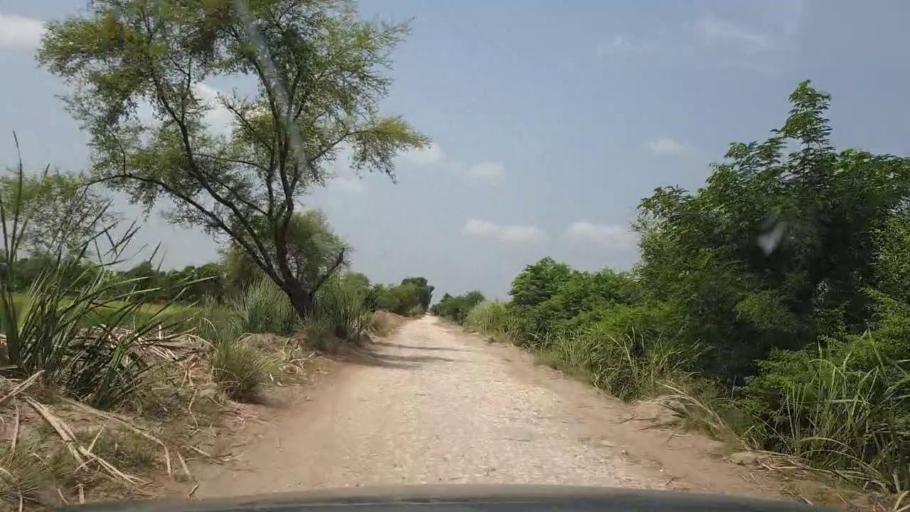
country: PK
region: Sindh
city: Ratodero
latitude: 27.8943
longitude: 68.3118
